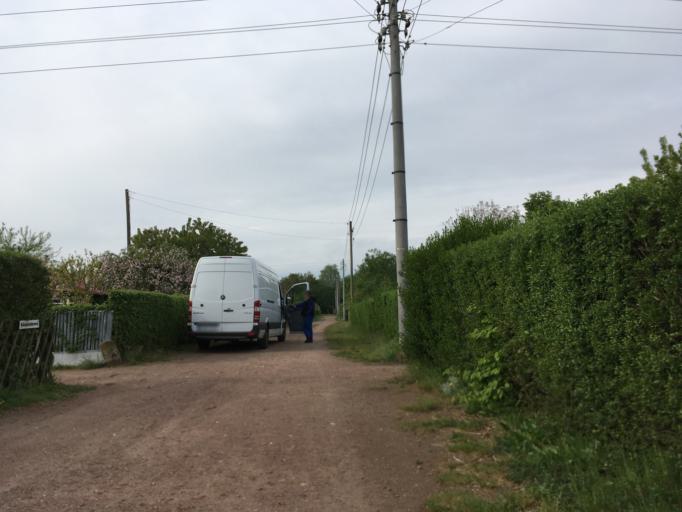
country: DE
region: Berlin
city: Stadtrandsiedlung Malchow
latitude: 52.5757
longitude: 13.4615
